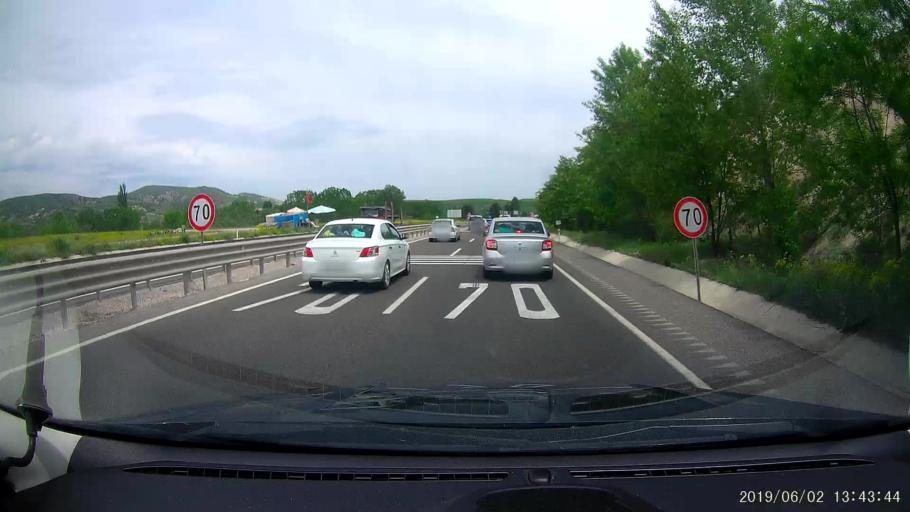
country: TR
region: Cankiri
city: Kursunlu
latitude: 40.8492
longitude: 33.2226
